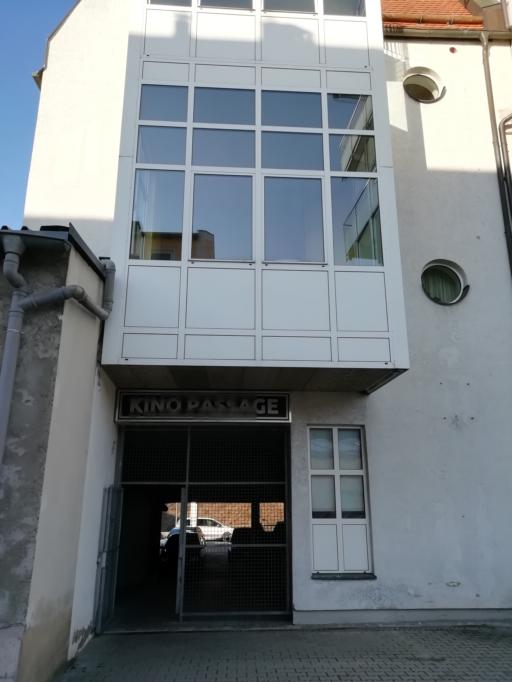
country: DE
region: Bavaria
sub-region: Upper Palatinate
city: Cham
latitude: 49.2197
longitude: 12.6655
